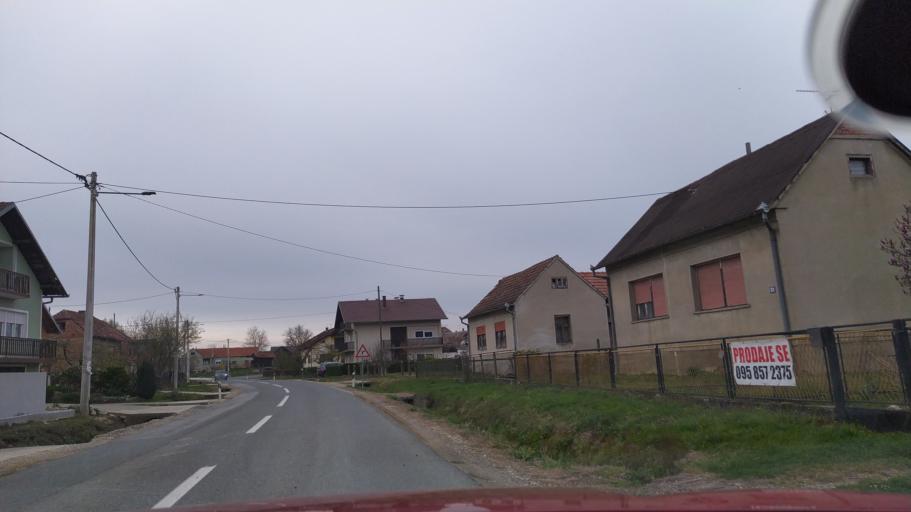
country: HR
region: Varazdinska
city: Ludbreg
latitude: 46.2357
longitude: 16.5475
